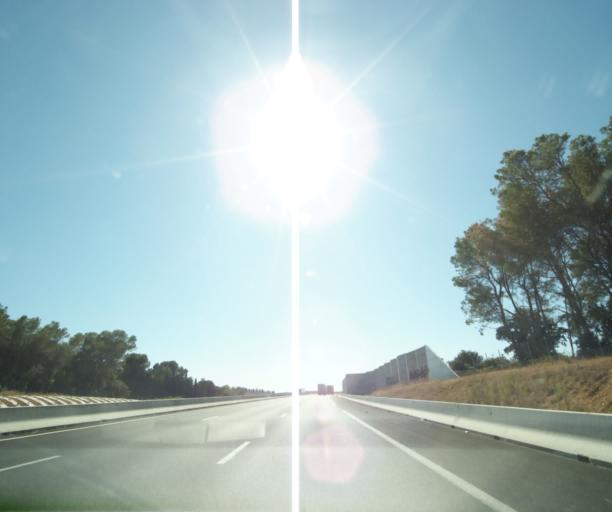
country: FR
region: Languedoc-Roussillon
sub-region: Departement de l'Herault
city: Saint-Aunes
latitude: 43.6079
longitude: 3.9455
